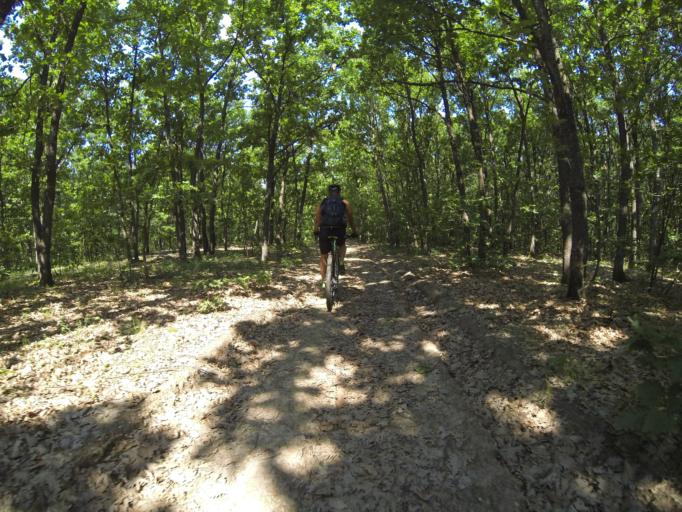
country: RO
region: Gorj
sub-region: Comuna Crusetu
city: Crusetu
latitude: 44.6145
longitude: 23.6401
